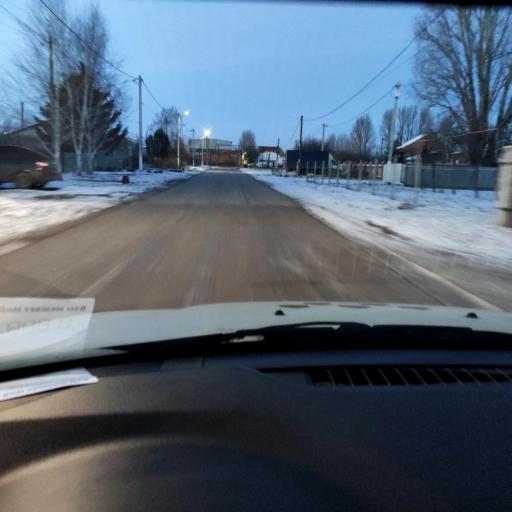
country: RU
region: Samara
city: Tol'yatti
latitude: 53.5677
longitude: 49.3905
